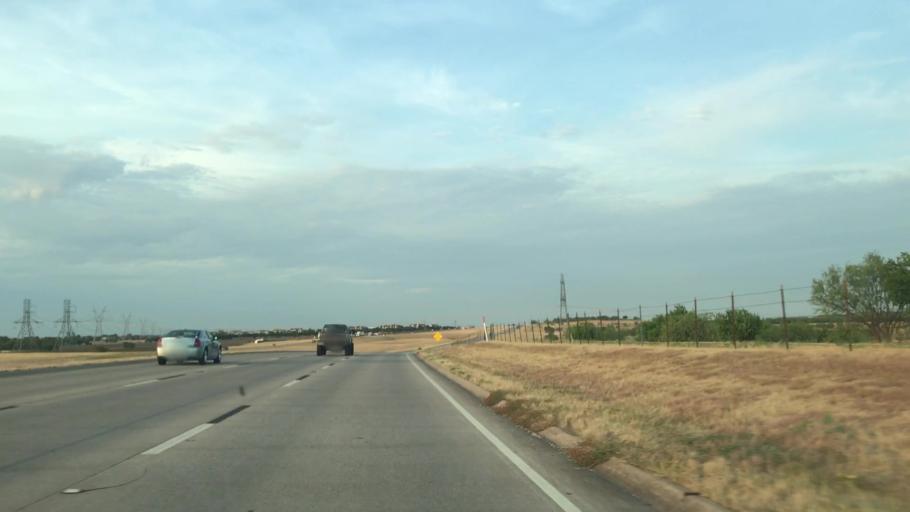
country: US
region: Texas
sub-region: Tarrant County
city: Haslet
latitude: 32.9649
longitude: -97.2957
